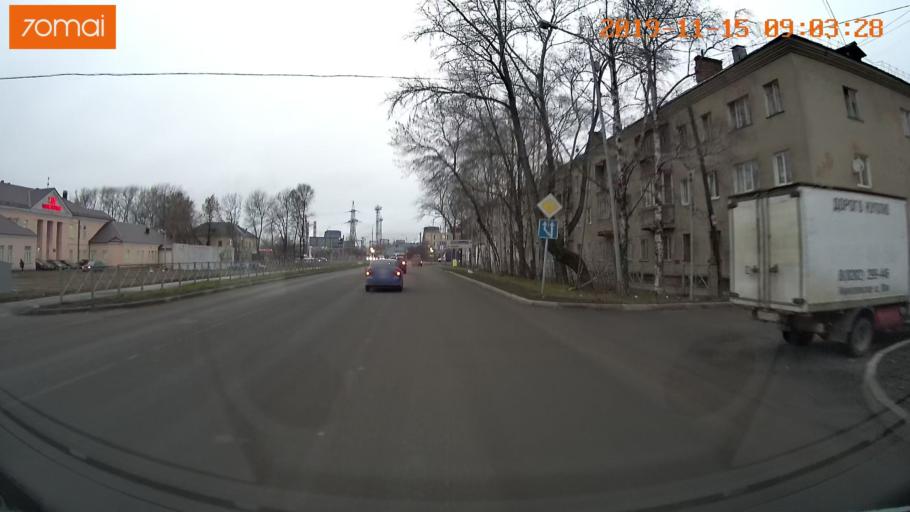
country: RU
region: Vologda
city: Cherepovets
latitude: 59.1386
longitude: 37.9213
